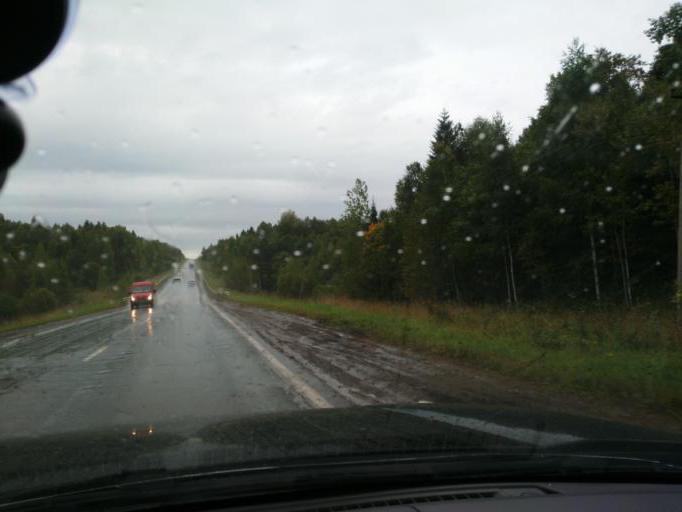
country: RU
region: Perm
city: Kultayevo
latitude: 57.8299
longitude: 55.8132
